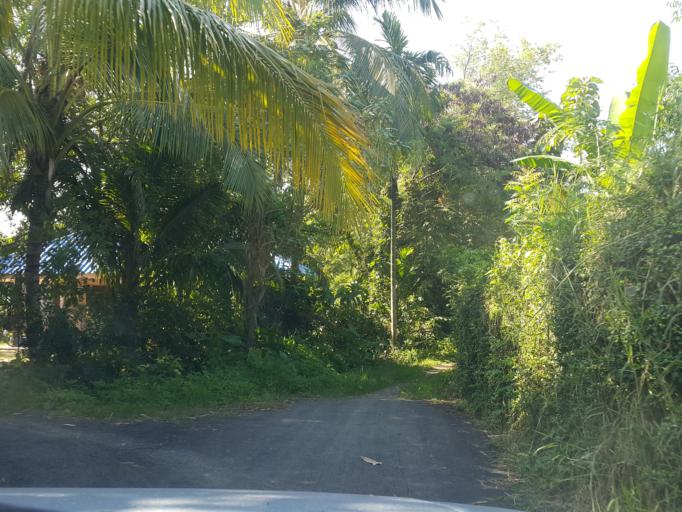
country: TH
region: Chiang Mai
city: Saraphi
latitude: 18.7407
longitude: 99.0523
